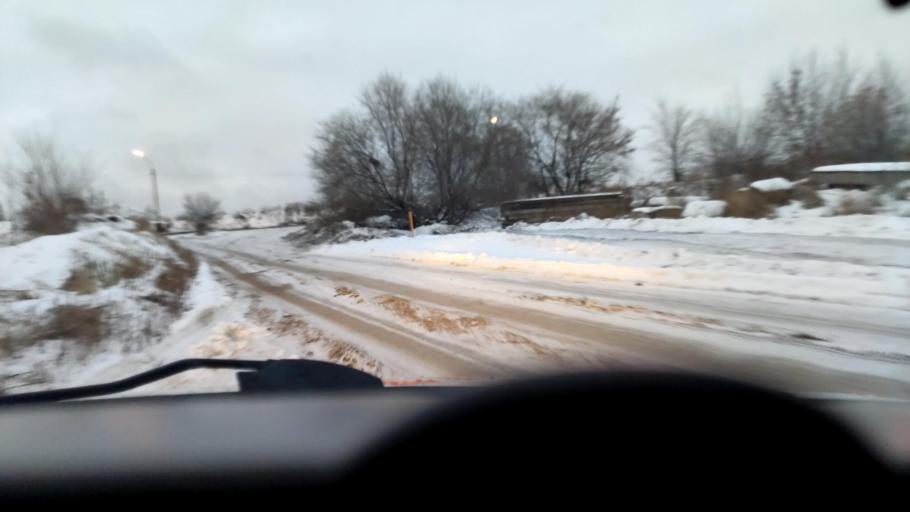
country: RU
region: Voronezj
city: Pridonskoy
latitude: 51.6981
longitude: 39.0720
